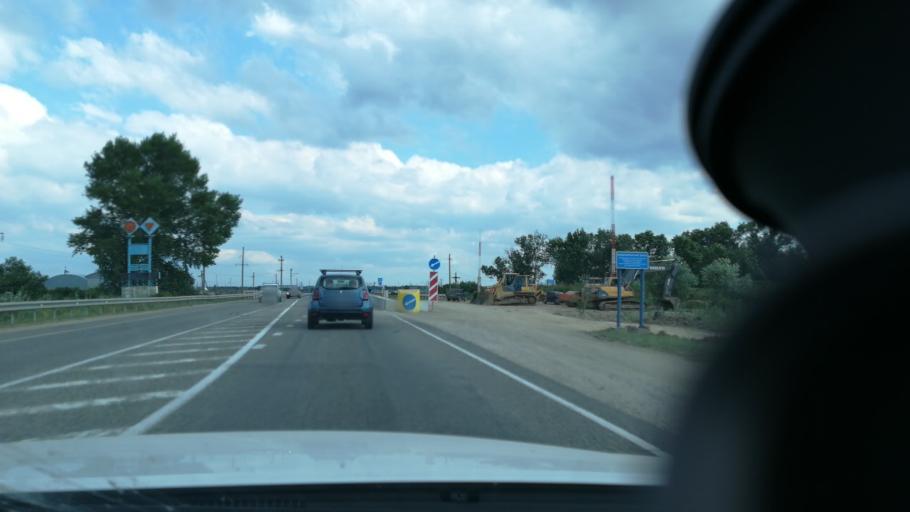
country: RU
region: Krasnodarskiy
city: Dzhiginka
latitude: 45.1482
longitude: 37.3098
